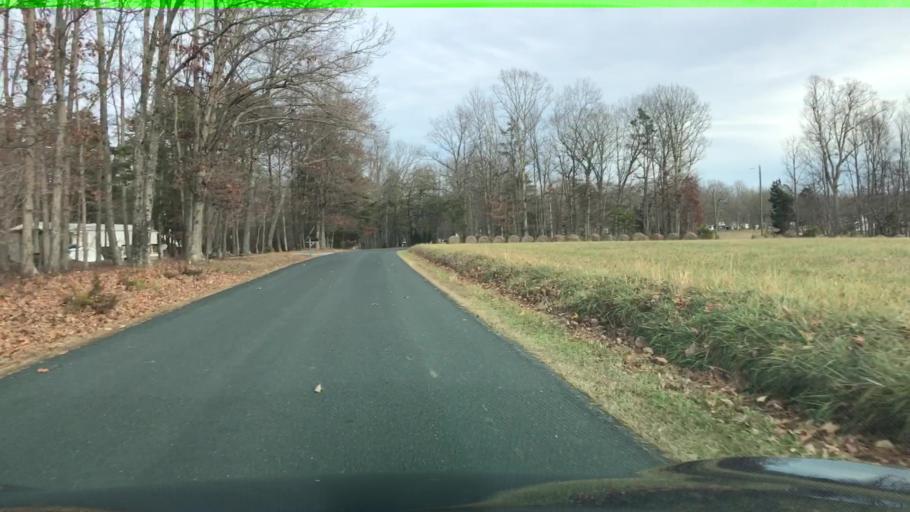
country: US
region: Virginia
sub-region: Campbell County
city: Concord
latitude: 37.2483
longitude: -78.8939
